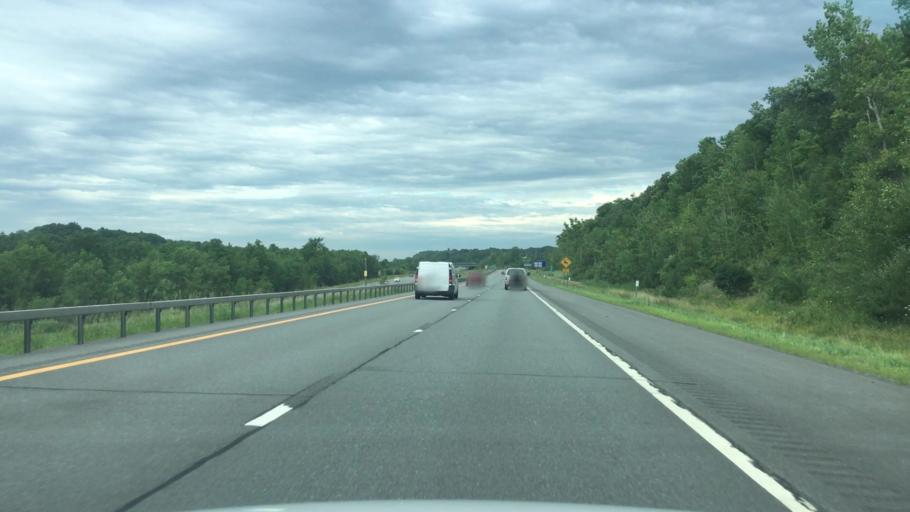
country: US
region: New York
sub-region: Albany County
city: Altamont
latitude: 42.7567
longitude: -74.1312
